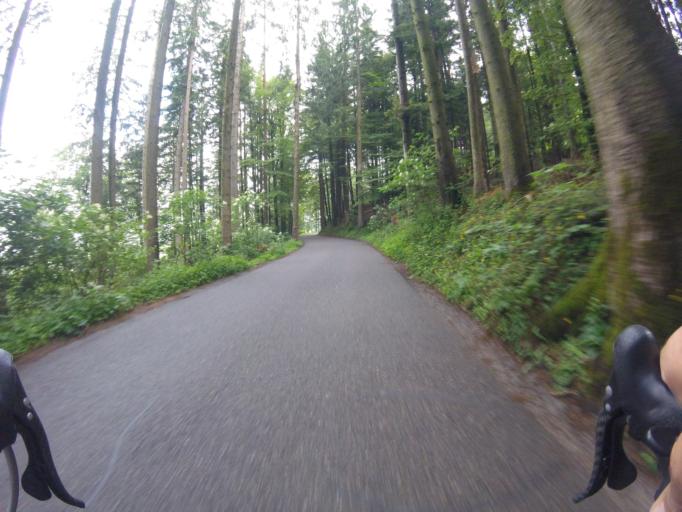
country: CH
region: Bern
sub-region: Bern-Mittelland District
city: Walkringen
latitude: 46.9670
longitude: 7.5973
